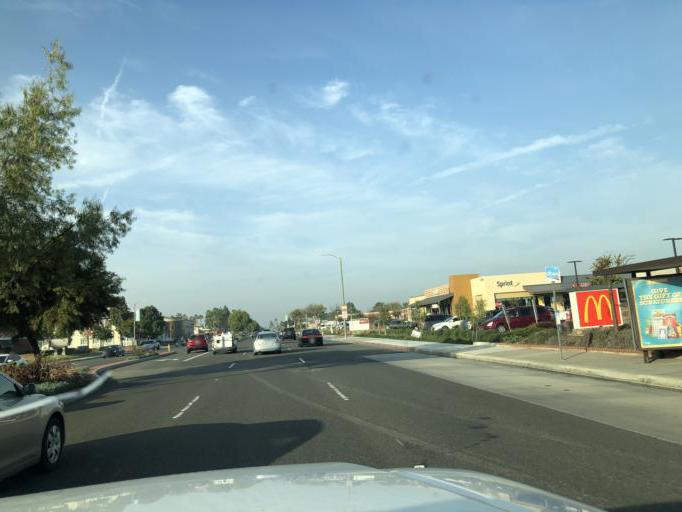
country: US
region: California
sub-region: Orange County
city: Fountain Valley
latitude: 33.6876
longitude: -117.9535
